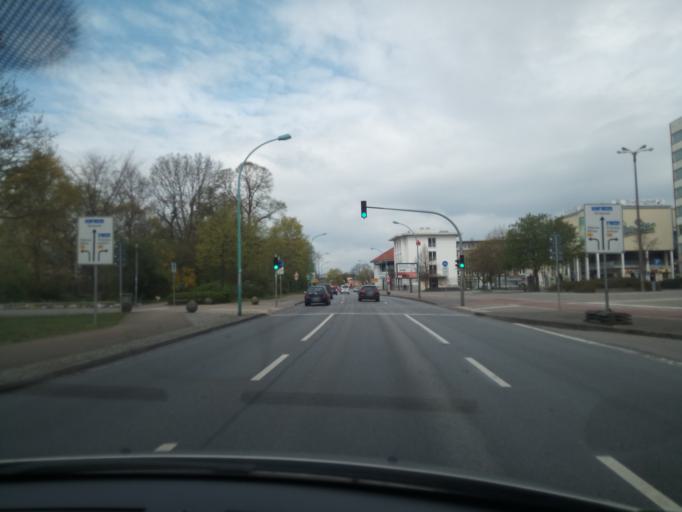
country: DE
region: Mecklenburg-Vorpommern
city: Neubrandenburg
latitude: 53.5566
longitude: 13.2669
